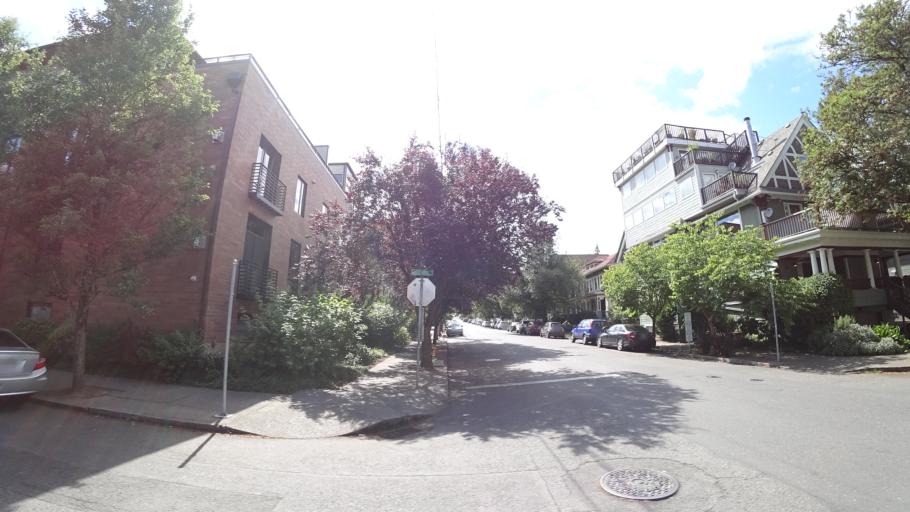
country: US
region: Oregon
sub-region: Multnomah County
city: Portland
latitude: 45.5269
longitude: -122.6964
